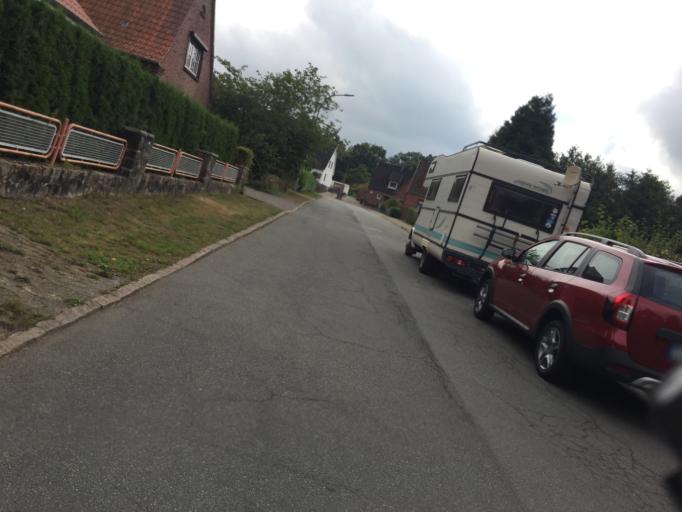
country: DE
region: Schleswig-Holstein
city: Munsterdorf
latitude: 53.9239
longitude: 9.5397
